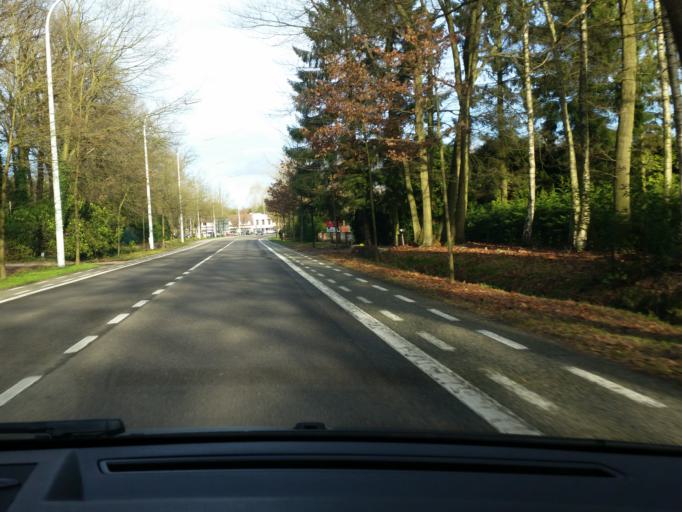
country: BE
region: Flanders
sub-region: Provincie Antwerpen
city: Brasschaat
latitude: 51.3352
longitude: 4.5258
